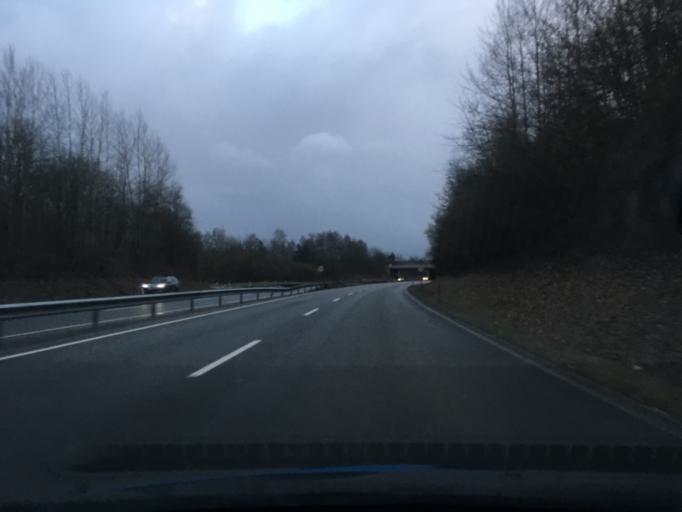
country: DE
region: Lower Saxony
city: Wendisch Evern
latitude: 53.2443
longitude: 10.4544
